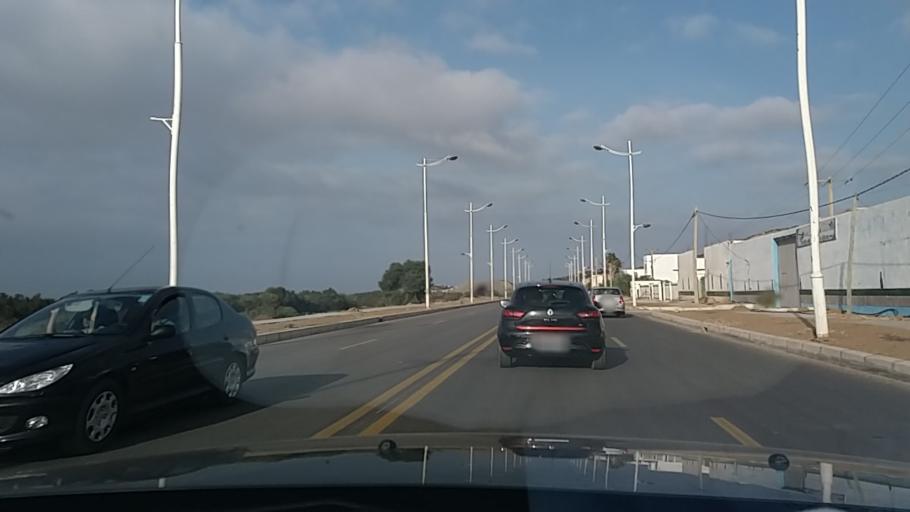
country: MA
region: Tanger-Tetouan
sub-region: Tetouan
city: Martil
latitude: 35.5761
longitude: -5.3104
